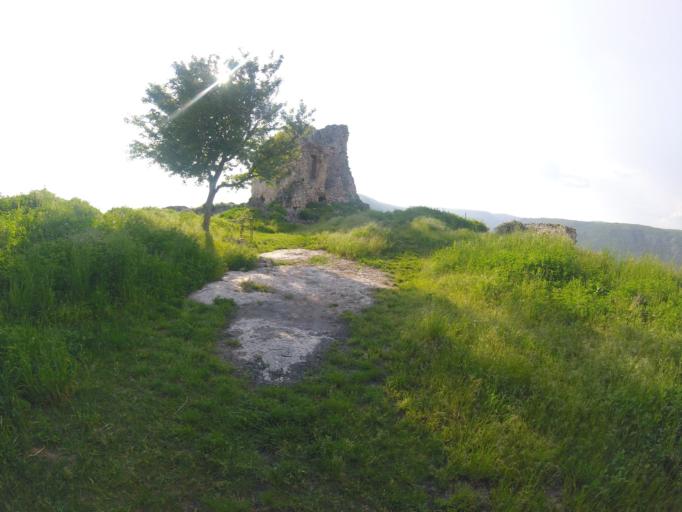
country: SK
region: Kosicky
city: Medzev
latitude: 48.6109
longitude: 20.8747
